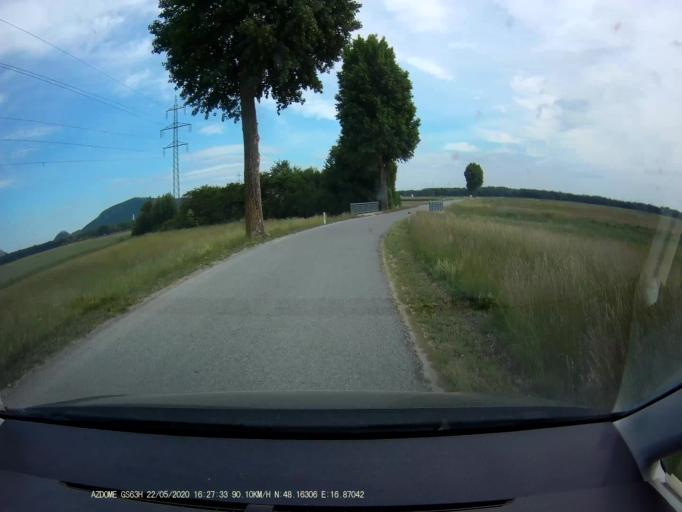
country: AT
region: Lower Austria
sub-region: Politischer Bezirk Ganserndorf
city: Engelhartstetten
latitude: 48.1627
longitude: 16.8706
